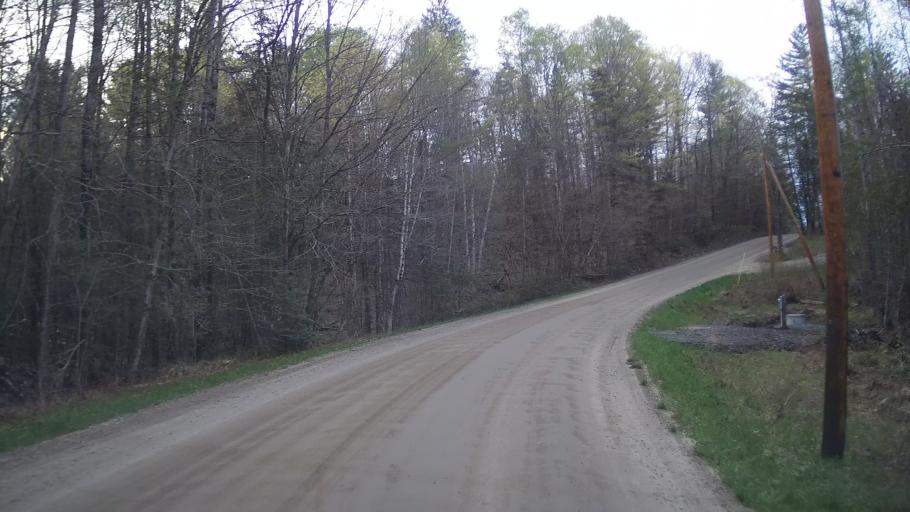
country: US
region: Vermont
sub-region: Caledonia County
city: Lyndonville
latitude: 44.5959
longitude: -71.9591
